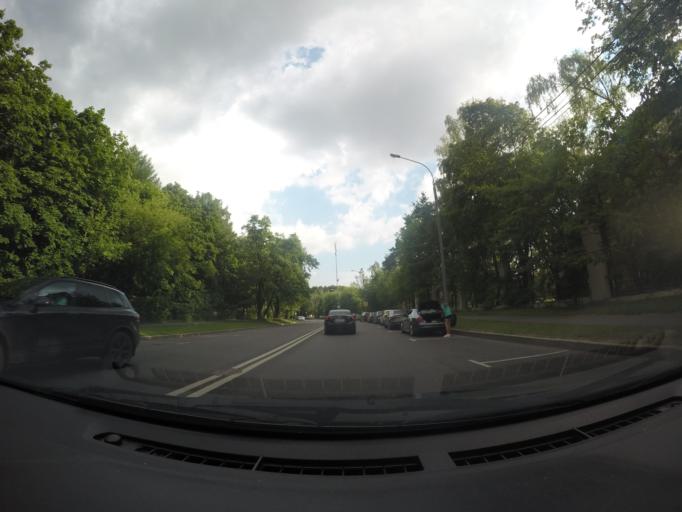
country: RU
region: Moscow
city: Sokol'niki
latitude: 55.8048
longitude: 37.6841
